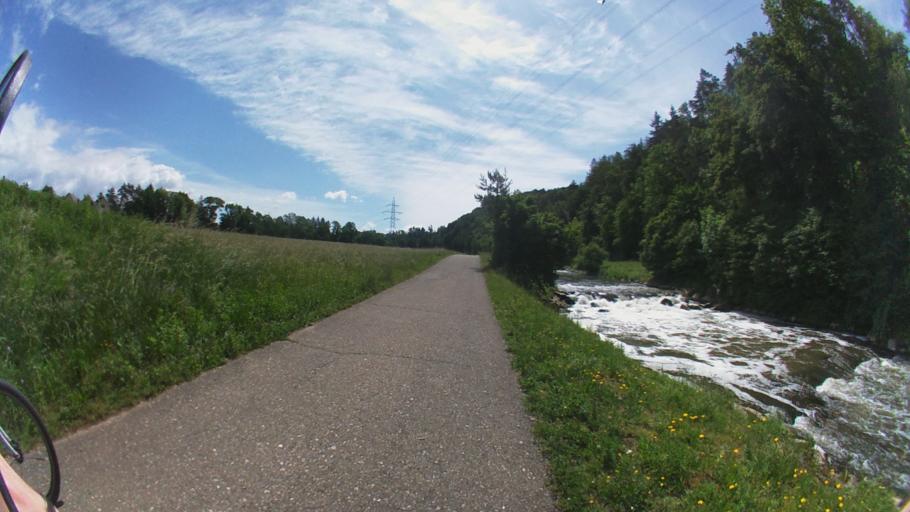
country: CH
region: Zurich
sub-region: Bezirk Buelach
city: Glattfelden
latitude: 47.5533
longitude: 8.5023
